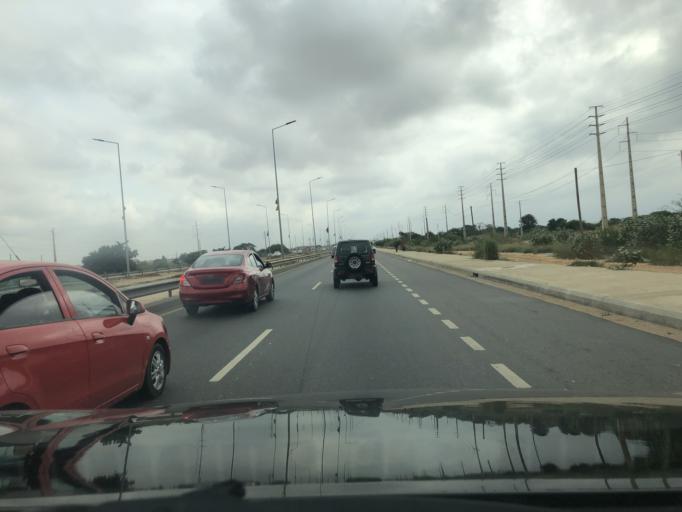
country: AO
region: Luanda
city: Luanda
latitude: -8.9515
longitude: 13.2592
